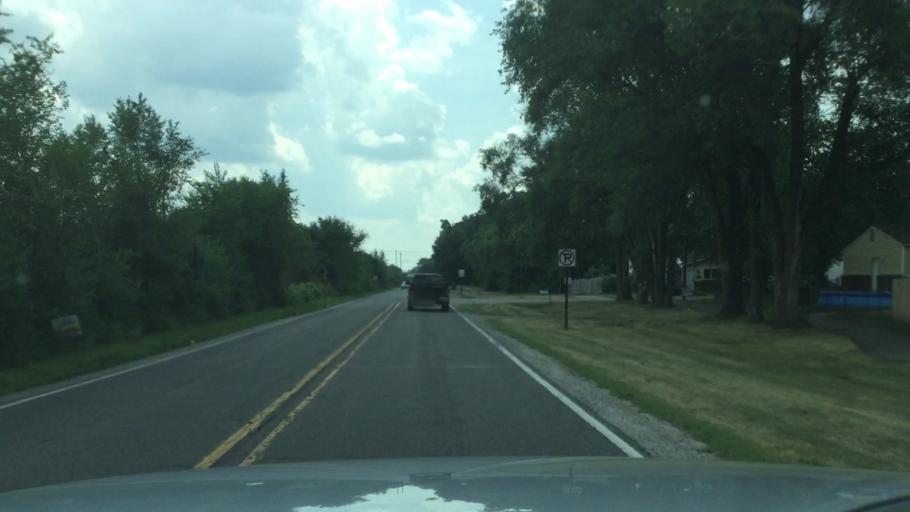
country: US
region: Michigan
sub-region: Washtenaw County
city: Ypsilanti
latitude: 42.2273
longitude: -83.5630
